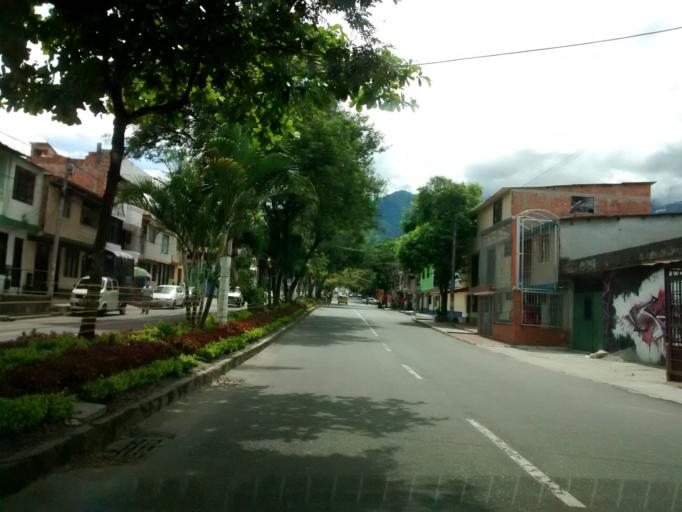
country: CO
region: Tolima
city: Ibague
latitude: 4.4323
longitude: -75.2001
